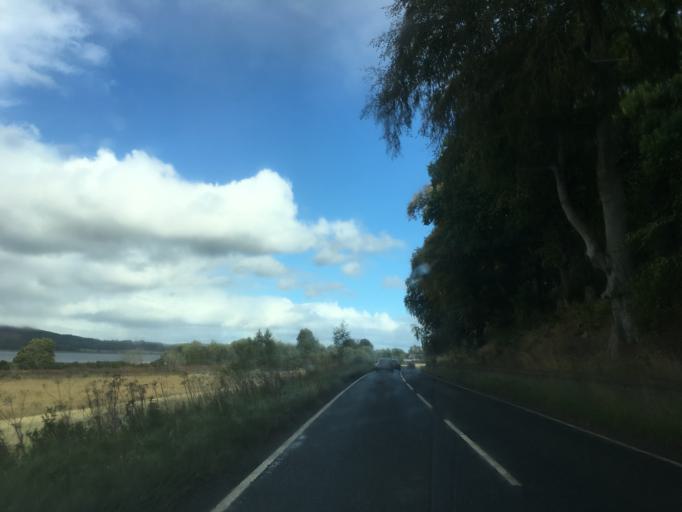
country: GB
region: Scotland
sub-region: Highland
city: Beauly
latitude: 57.4779
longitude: -4.3693
